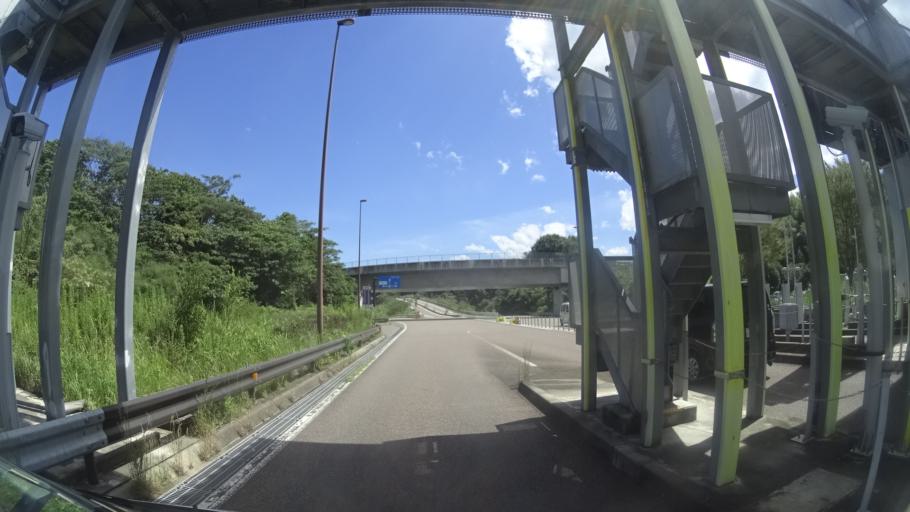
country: JP
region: Gifu
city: Minokamo
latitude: 35.4712
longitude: 137.0247
